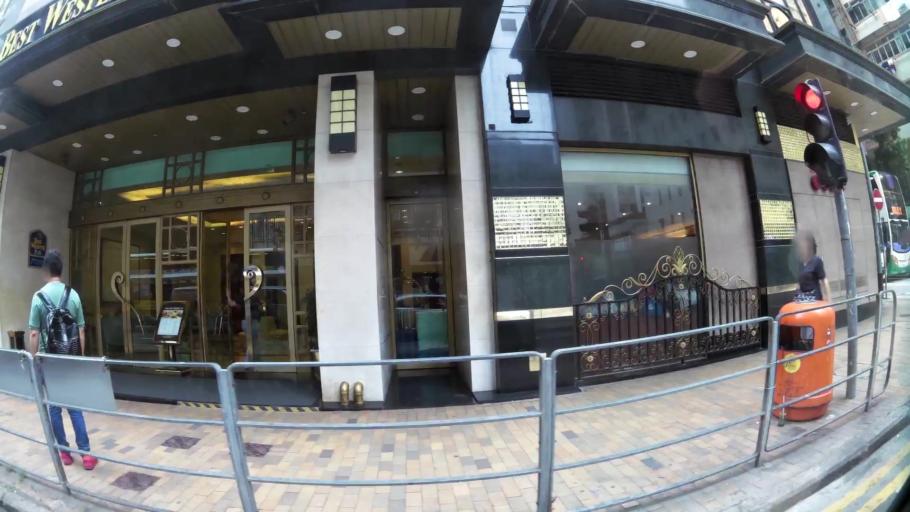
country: HK
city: Hong Kong
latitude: 22.2875
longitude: 114.1390
